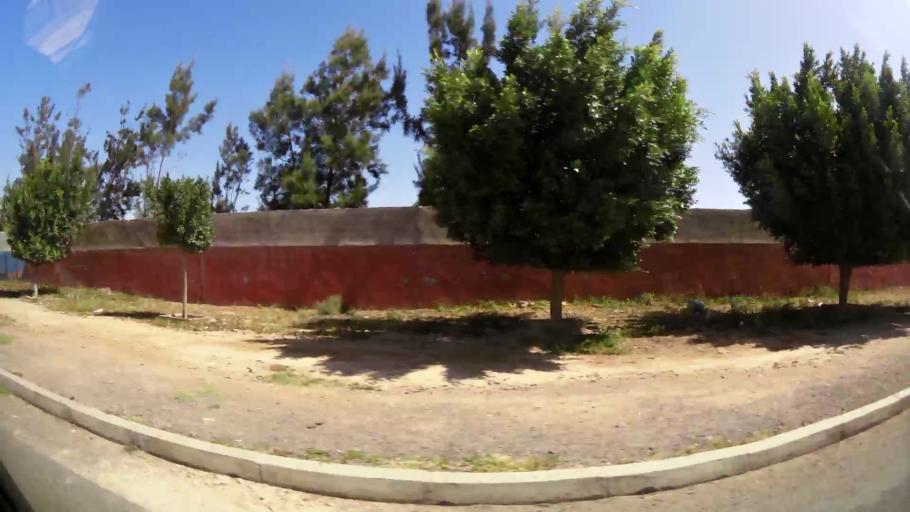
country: MA
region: Souss-Massa-Draa
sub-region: Inezgane-Ait Mellou
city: Inezgane
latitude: 30.3264
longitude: -9.5057
